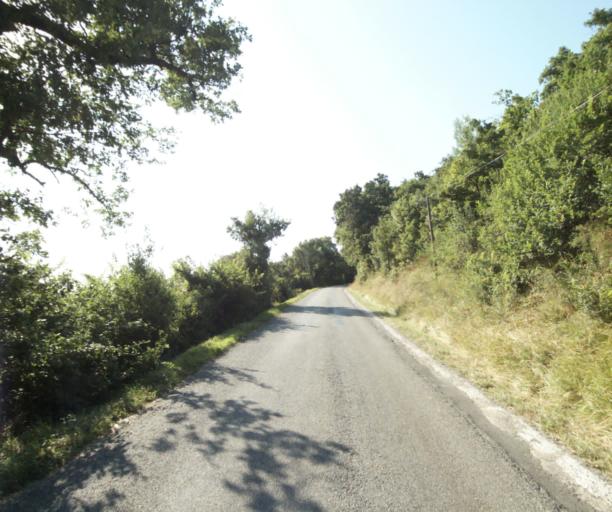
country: FR
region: Midi-Pyrenees
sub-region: Departement de la Haute-Garonne
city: Saint-Felix-Lauragais
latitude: 43.4416
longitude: 1.8200
